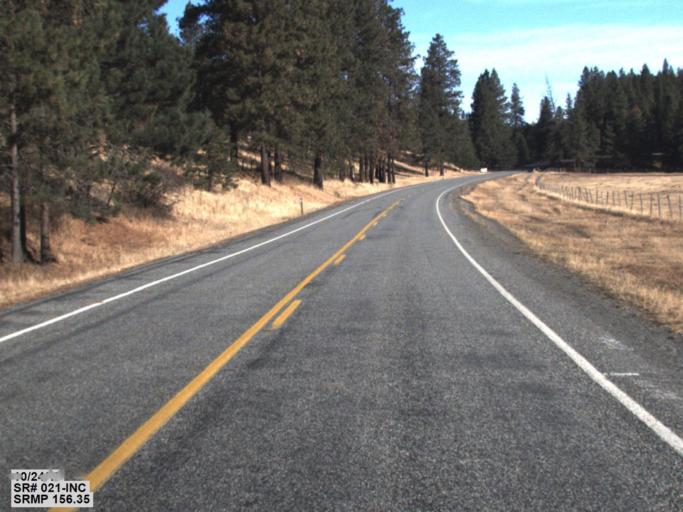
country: US
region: Washington
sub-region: Ferry County
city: Republic
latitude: 48.5890
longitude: -118.7424
